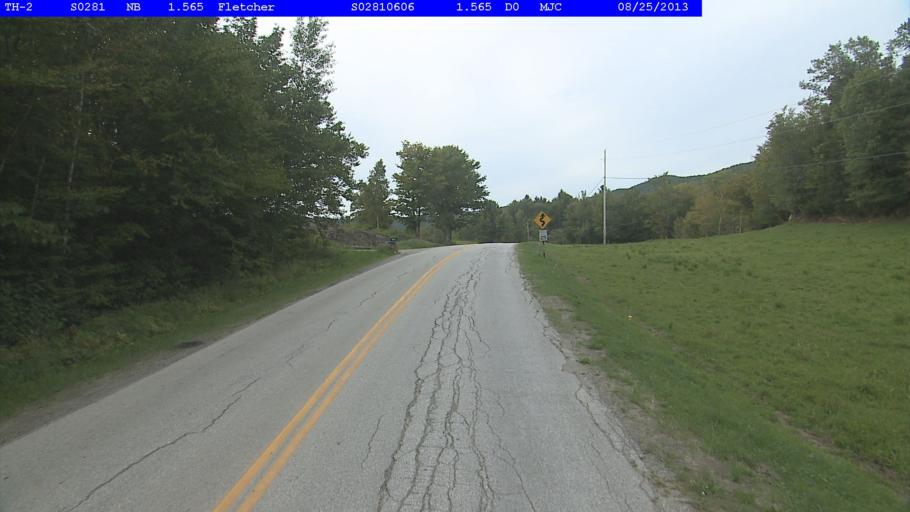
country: US
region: Vermont
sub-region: Chittenden County
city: Milton
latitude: 44.6977
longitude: -72.9354
